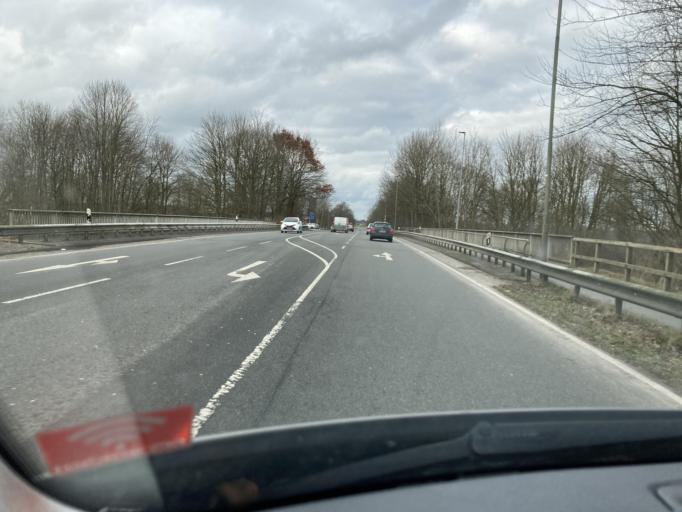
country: DE
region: Lower Saxony
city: Fedderwarden
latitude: 53.5591
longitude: 8.0800
